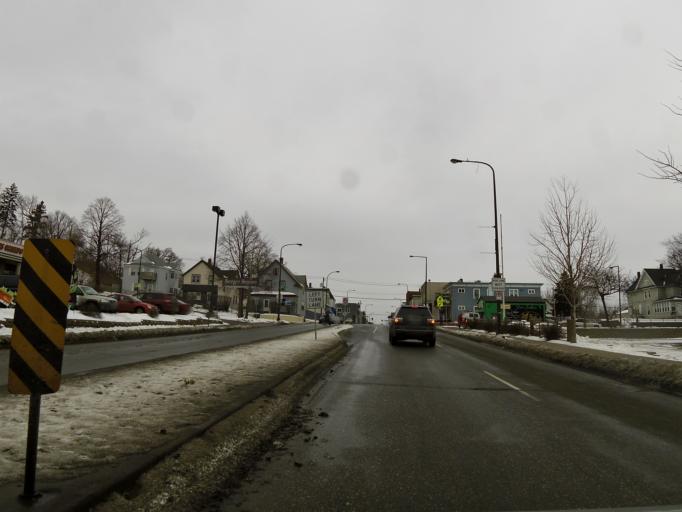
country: US
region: Minnesota
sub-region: Ramsey County
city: Saint Paul
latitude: 44.9679
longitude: -93.0660
